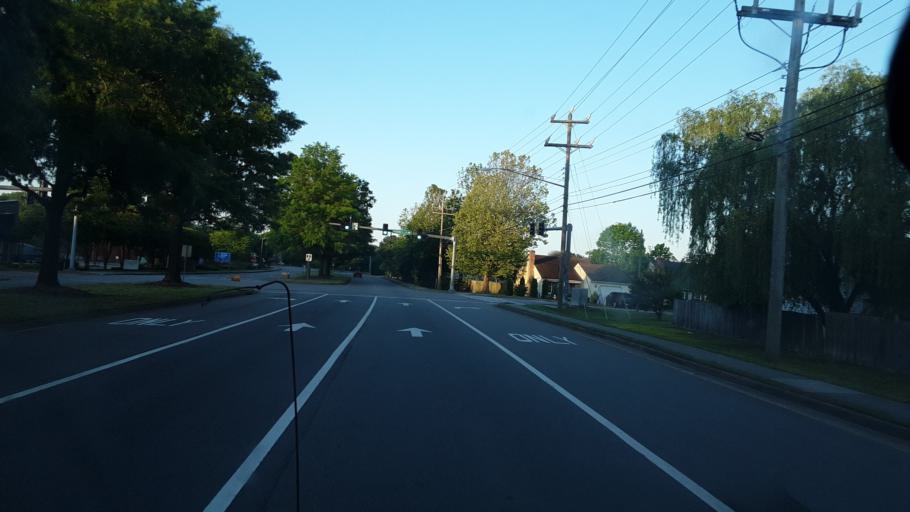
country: US
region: Virginia
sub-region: City of Virginia Beach
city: Virginia Beach
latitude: 36.7831
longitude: -76.0011
